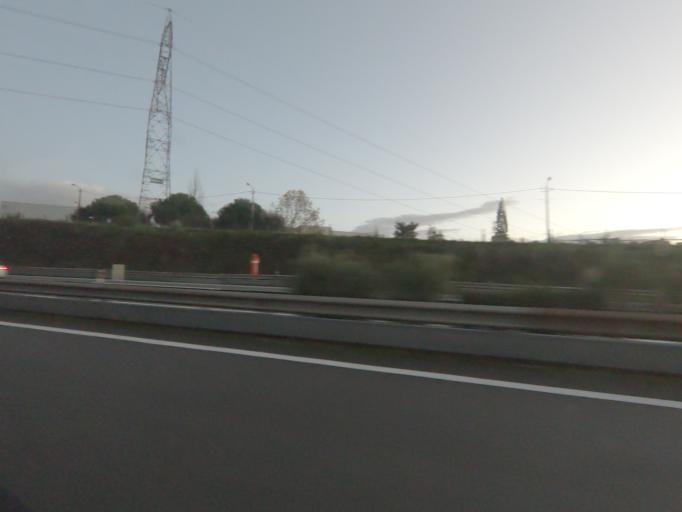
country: PT
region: Porto
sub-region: Paredes
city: Recarei
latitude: 41.1726
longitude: -8.4309
